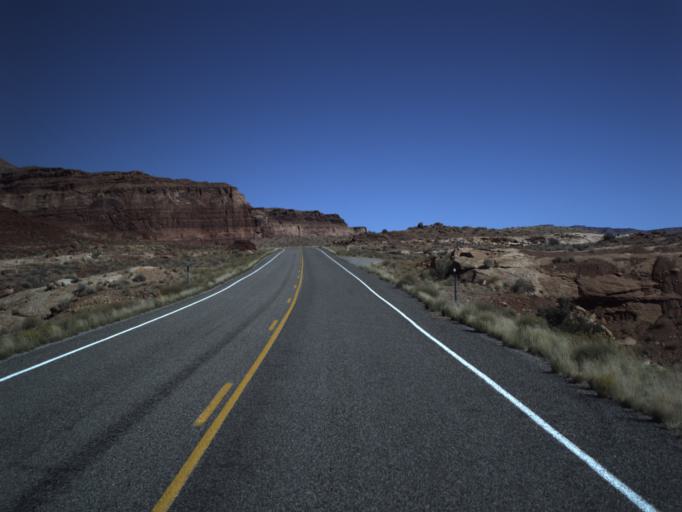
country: US
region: Utah
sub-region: San Juan County
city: Blanding
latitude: 37.9111
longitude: -110.3992
